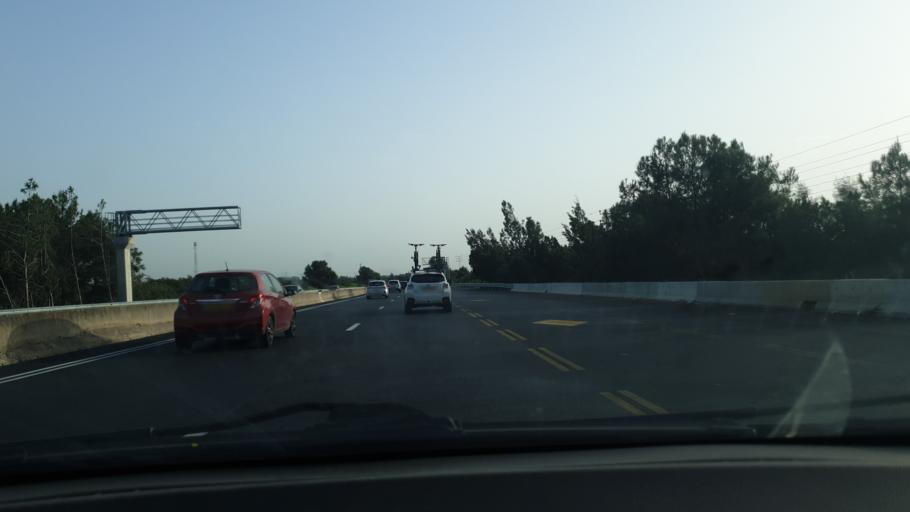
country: IL
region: Central District
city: Tel Mond
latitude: 32.2321
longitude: 34.8843
